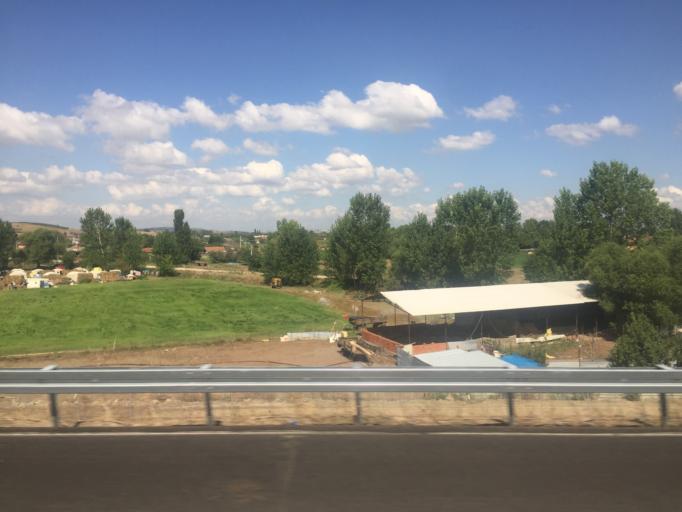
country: TR
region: Balikesir
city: Gobel
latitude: 40.0560
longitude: 28.2362
